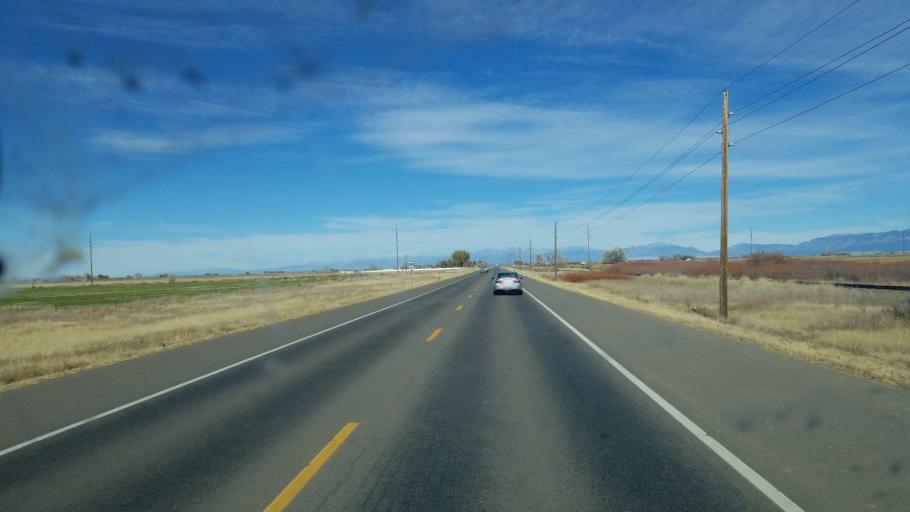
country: US
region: Colorado
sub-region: Alamosa County
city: Alamosa
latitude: 37.3826
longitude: -105.9158
